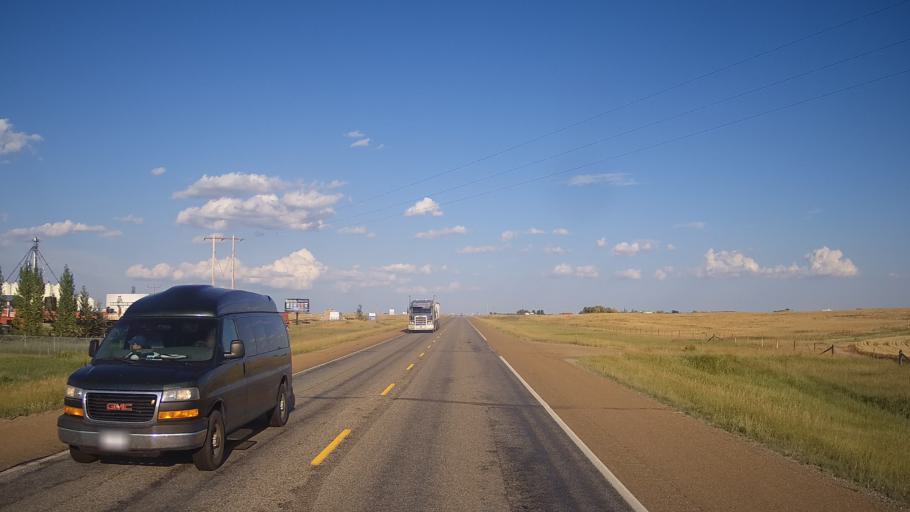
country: CA
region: Alberta
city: Hanna
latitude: 51.6326
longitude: -111.9314
